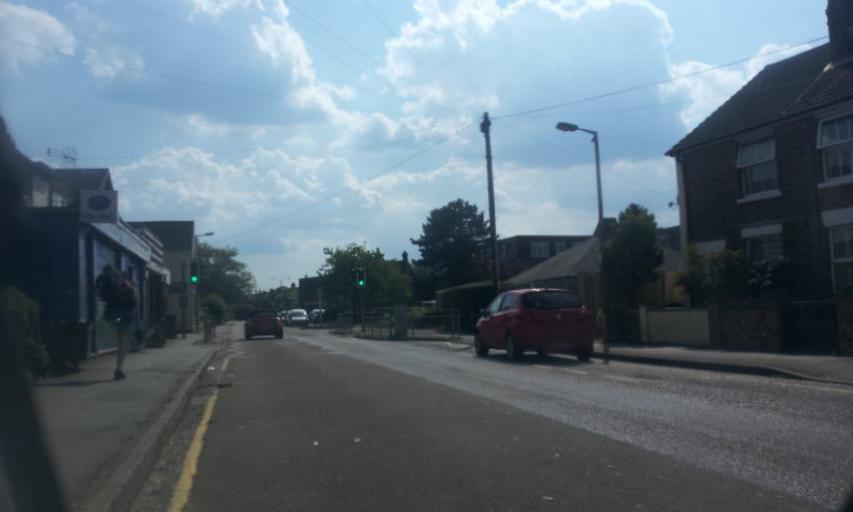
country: GB
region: England
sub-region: Kent
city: Paddock Wood
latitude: 51.1794
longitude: 0.3869
